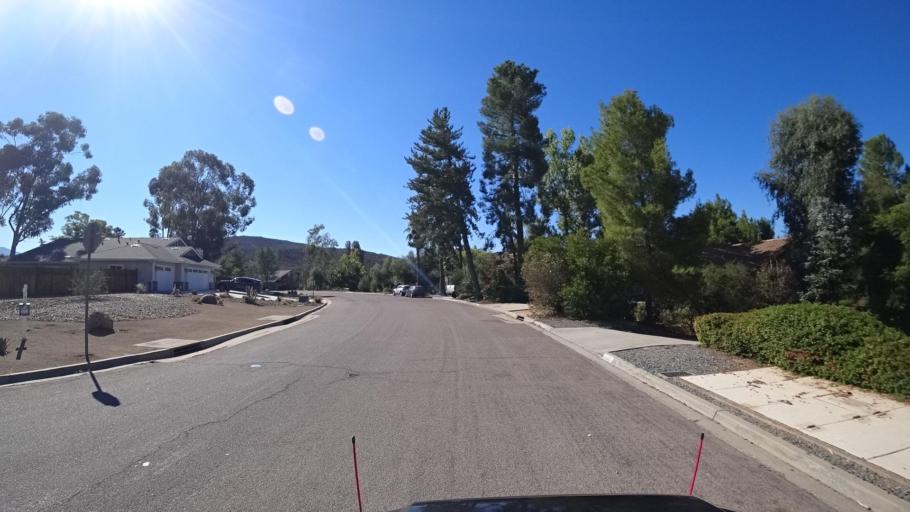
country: US
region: California
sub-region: San Diego County
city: San Diego Country Estates
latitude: 33.0011
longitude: -116.7681
